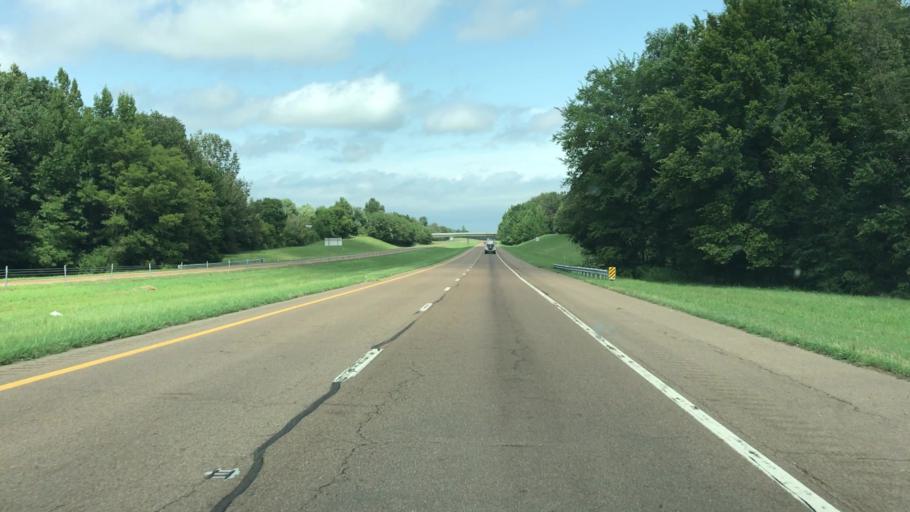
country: US
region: Tennessee
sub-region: Obion County
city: Union City
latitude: 36.4482
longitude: -89.0044
